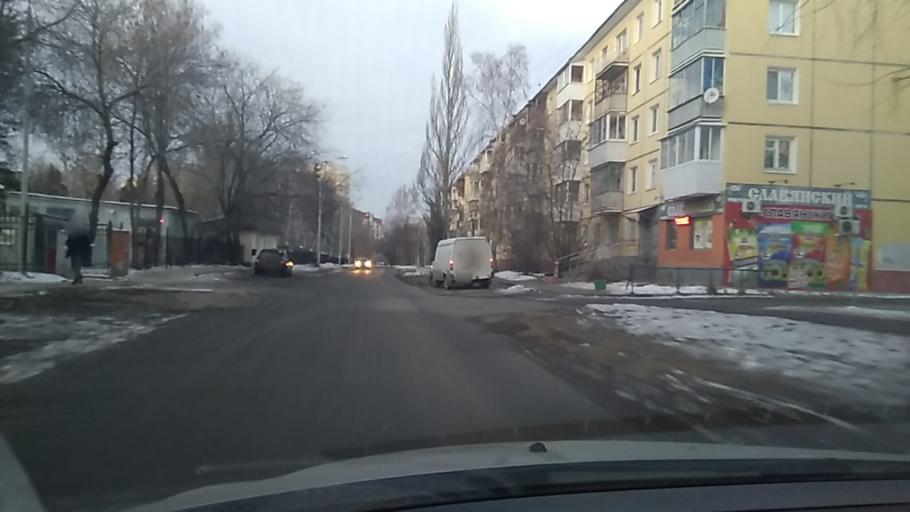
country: RU
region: Sverdlovsk
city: Istok
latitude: 56.7639
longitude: 60.7109
